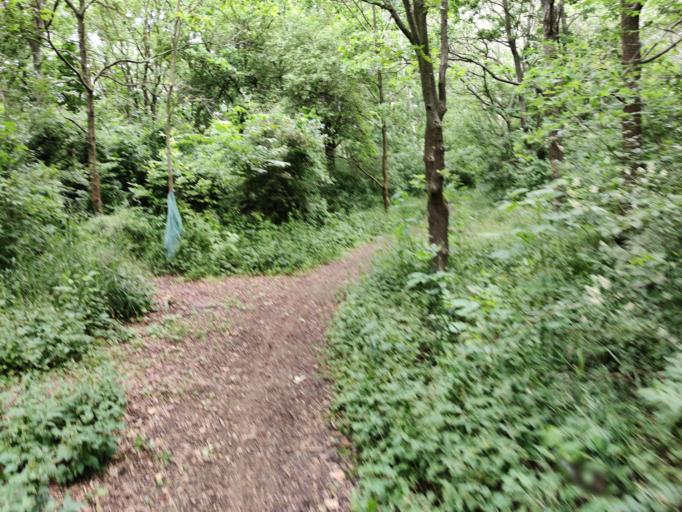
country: HU
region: Hajdu-Bihar
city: Balmazujvaros
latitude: 47.6145
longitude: 21.3302
